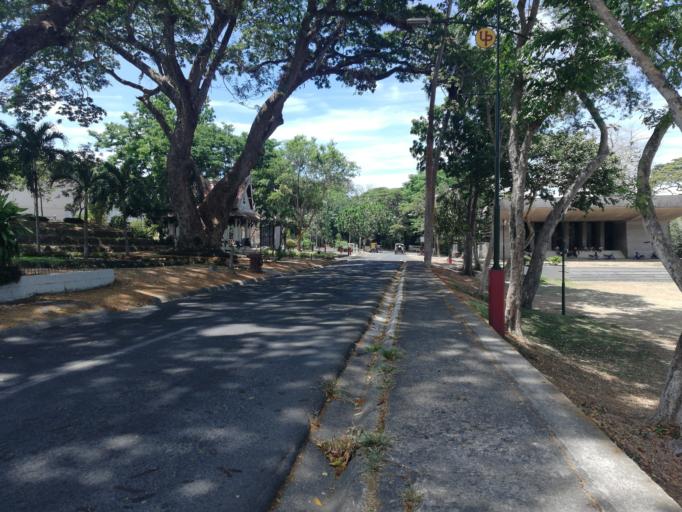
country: PH
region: Calabarzon
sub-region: Province of Laguna
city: Los Banos
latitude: 14.1629
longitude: 121.2404
